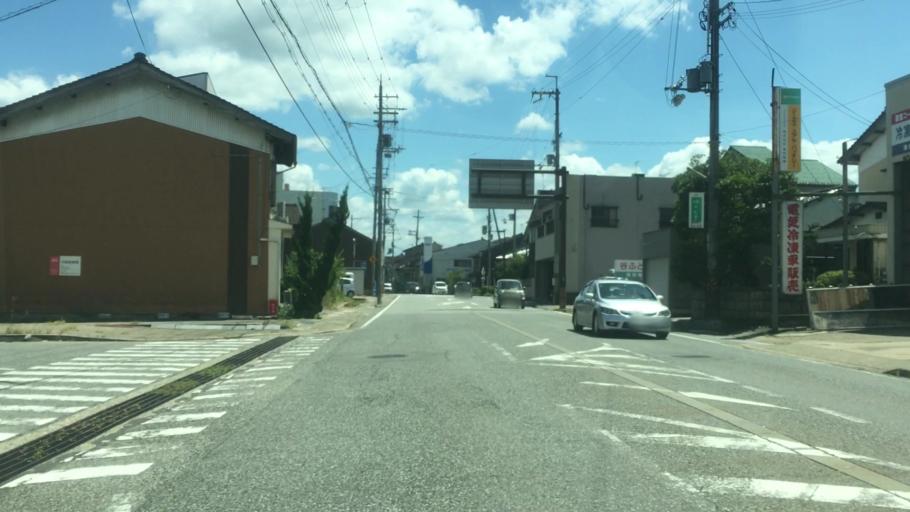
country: JP
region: Hyogo
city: Toyooka
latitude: 35.5399
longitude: 134.8242
